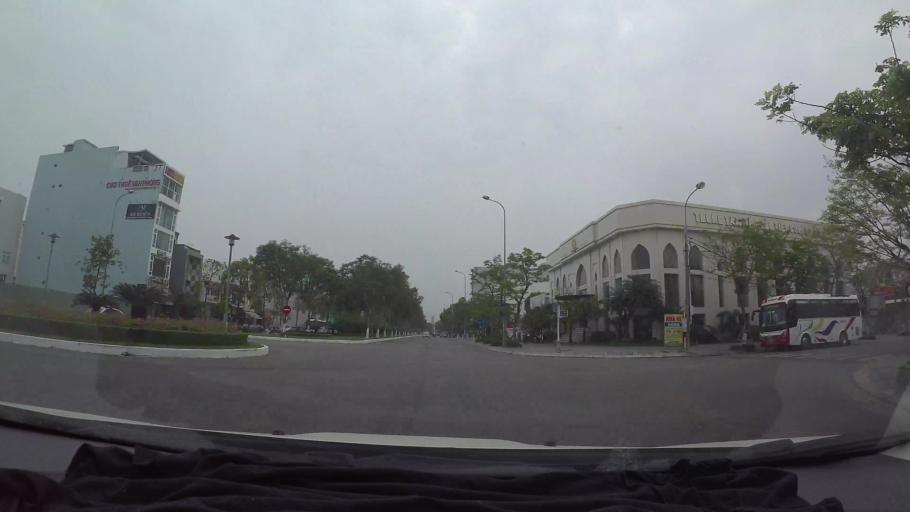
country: VN
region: Da Nang
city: Cam Le
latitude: 16.0400
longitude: 108.2156
